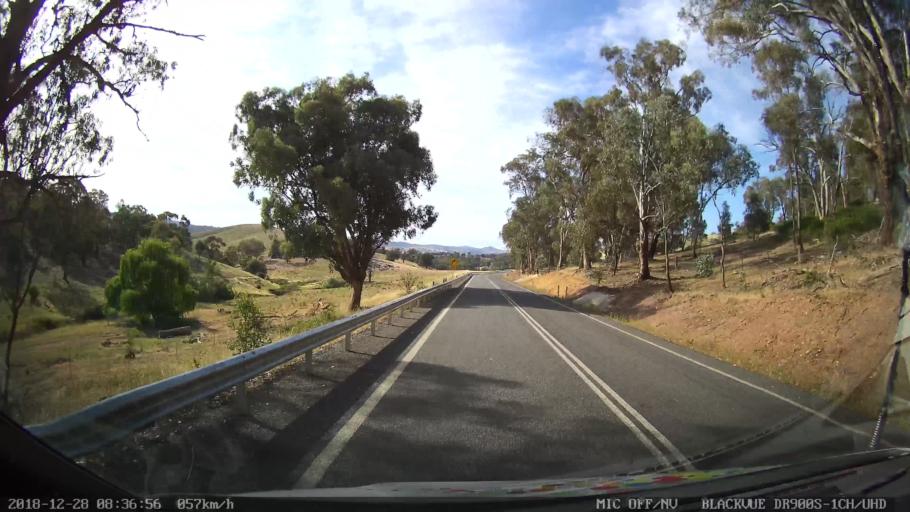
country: AU
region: New South Wales
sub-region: Blayney
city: Blayney
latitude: -33.9911
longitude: 149.3128
